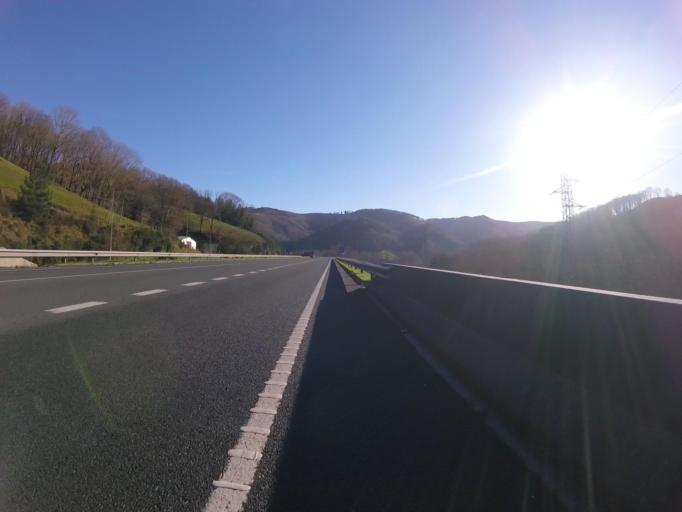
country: ES
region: Navarre
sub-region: Provincia de Navarra
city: Bera
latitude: 43.2812
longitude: -1.7118
